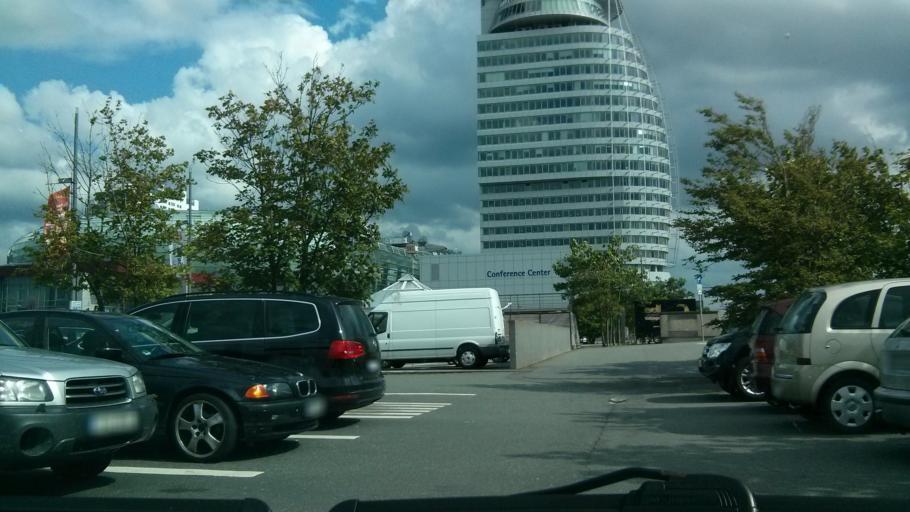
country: DE
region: Bremen
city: Bremerhaven
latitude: 53.5443
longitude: 8.5720
